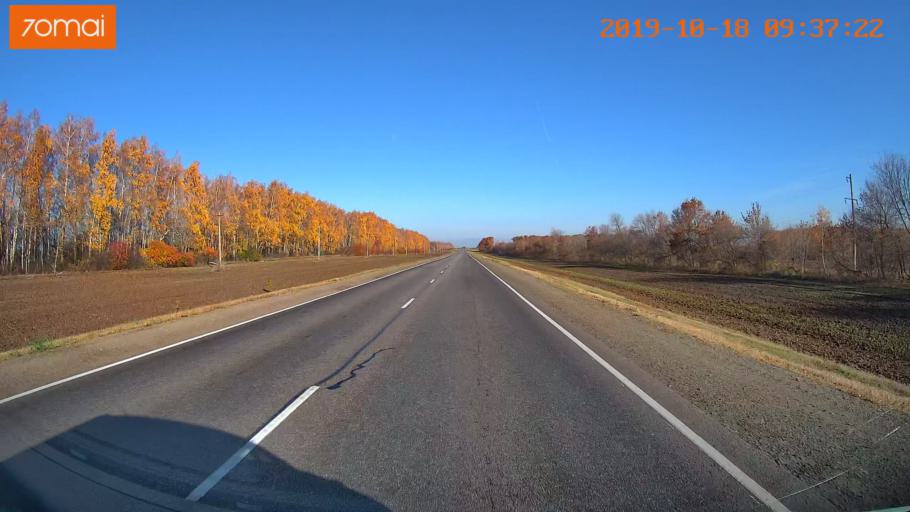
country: RU
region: Tula
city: Yefremov
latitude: 53.2212
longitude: 38.1413
